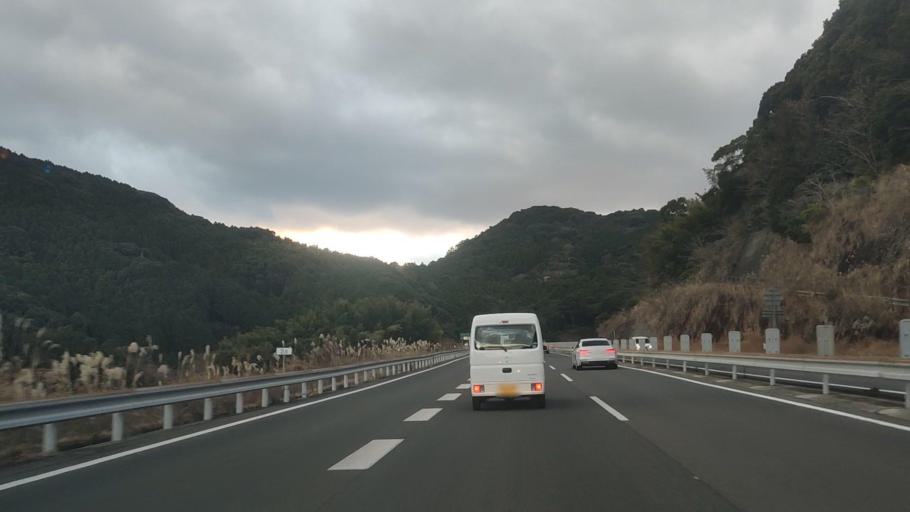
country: JP
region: Nagasaki
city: Obita
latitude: 32.8165
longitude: 129.9478
